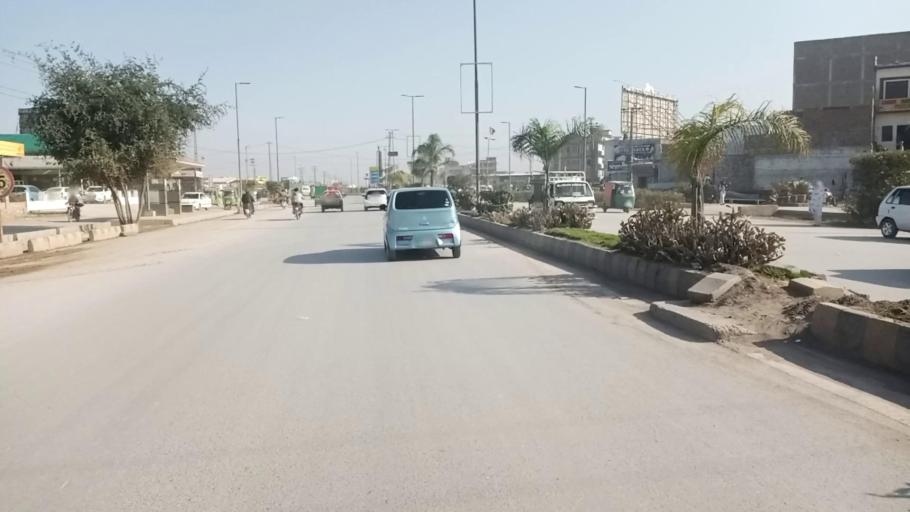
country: PK
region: Khyber Pakhtunkhwa
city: Peshawar
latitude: 34.0328
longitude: 71.6050
